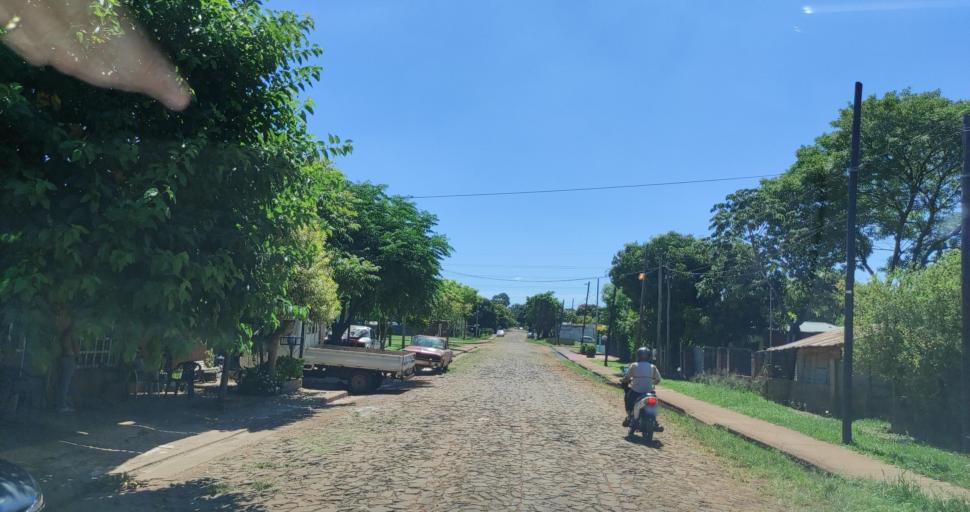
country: AR
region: Misiones
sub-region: Departamento de Capital
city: Posadas
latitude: -27.4131
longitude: -55.9074
